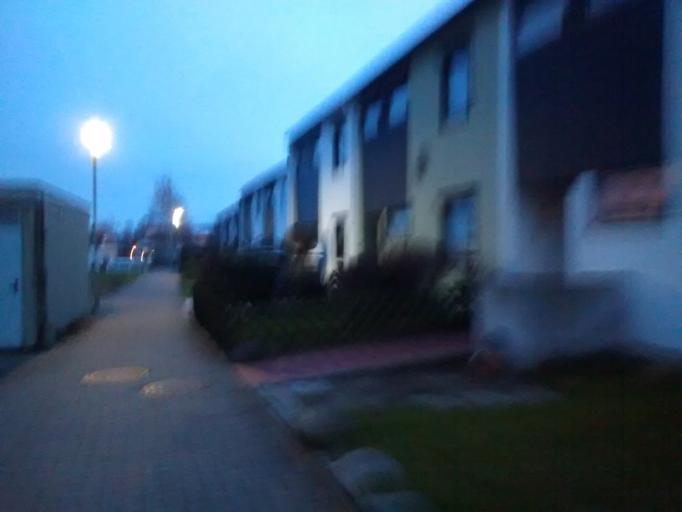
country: DE
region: Lower Saxony
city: Wolfenbuettel
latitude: 52.1674
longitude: 10.5227
